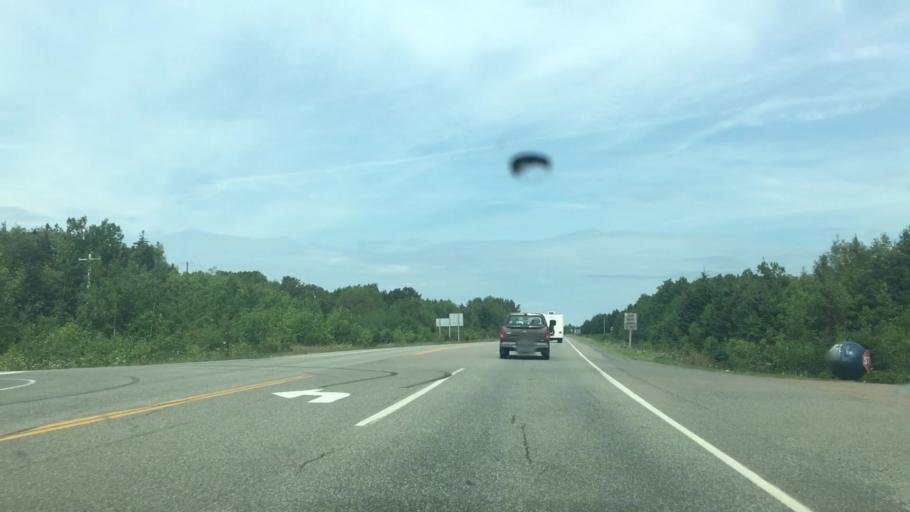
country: CA
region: Nova Scotia
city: Port Hawkesbury
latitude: 45.6576
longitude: -61.4506
